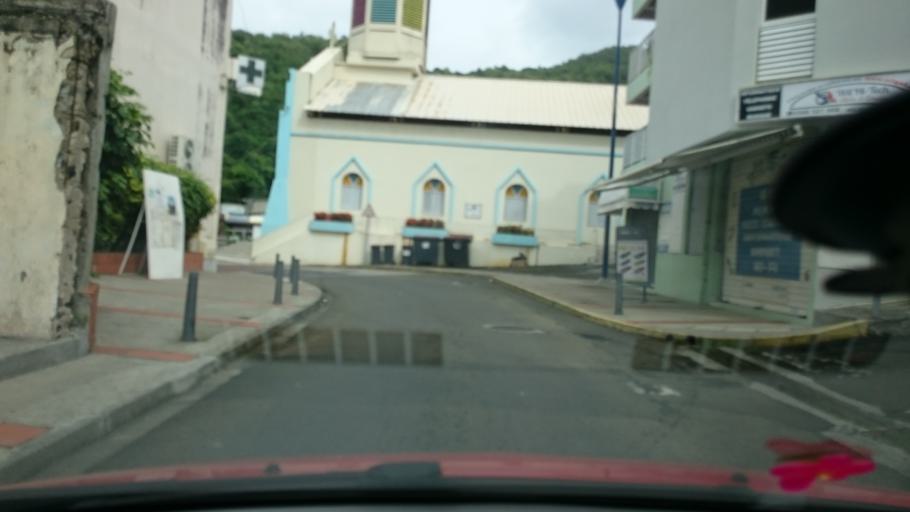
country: MQ
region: Martinique
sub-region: Martinique
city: Riviere-Pilote
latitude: 14.4868
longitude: -60.9035
